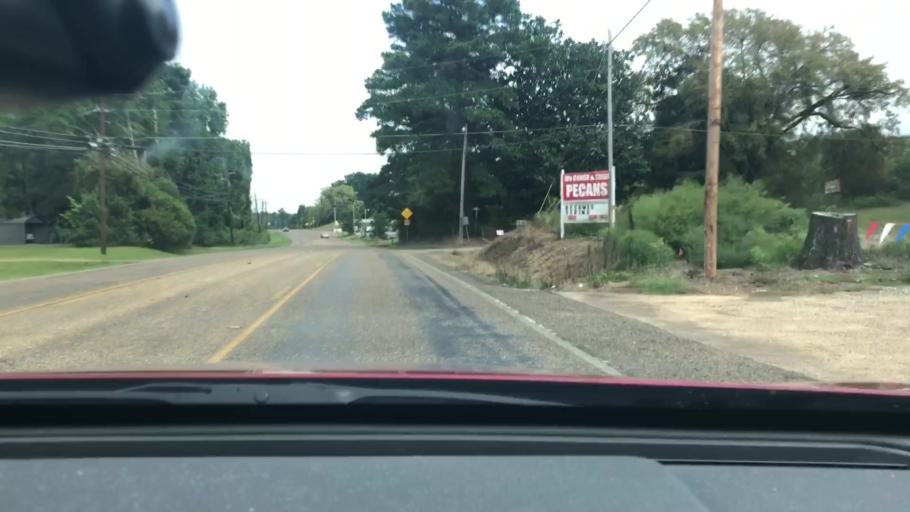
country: US
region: Texas
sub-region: Bowie County
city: Nash
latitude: 33.4427
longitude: -94.1142
